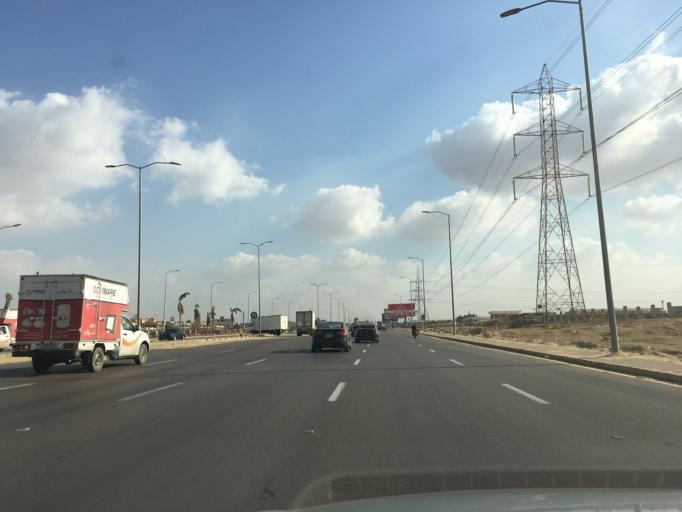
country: EG
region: Al Jizah
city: Awsim
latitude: 30.0245
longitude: 30.9680
